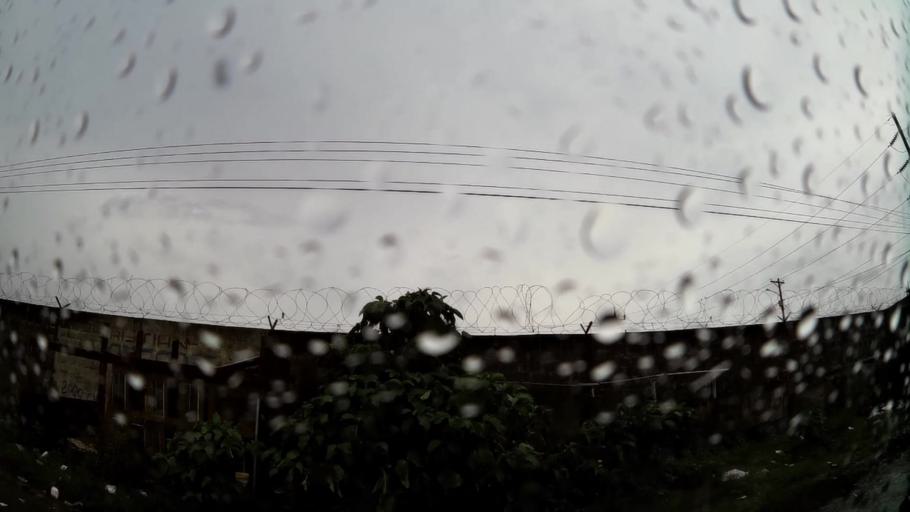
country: PA
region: Colon
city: Arco Iris
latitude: 9.3400
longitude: -79.8933
